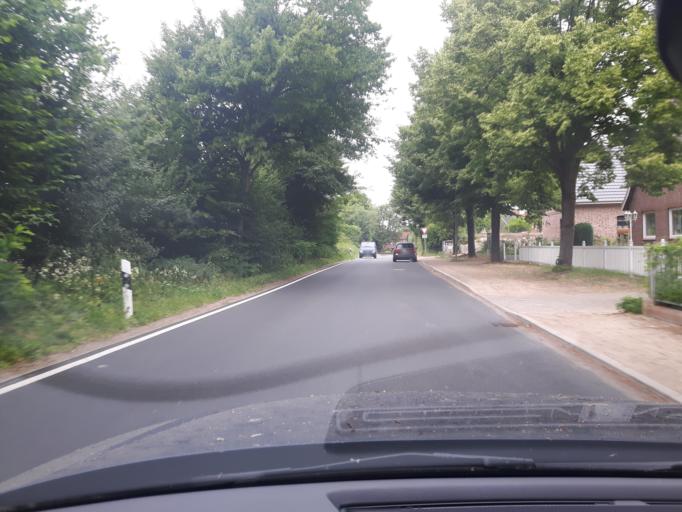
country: DE
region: Schleswig-Holstein
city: Ratekau
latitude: 53.9345
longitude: 10.7835
